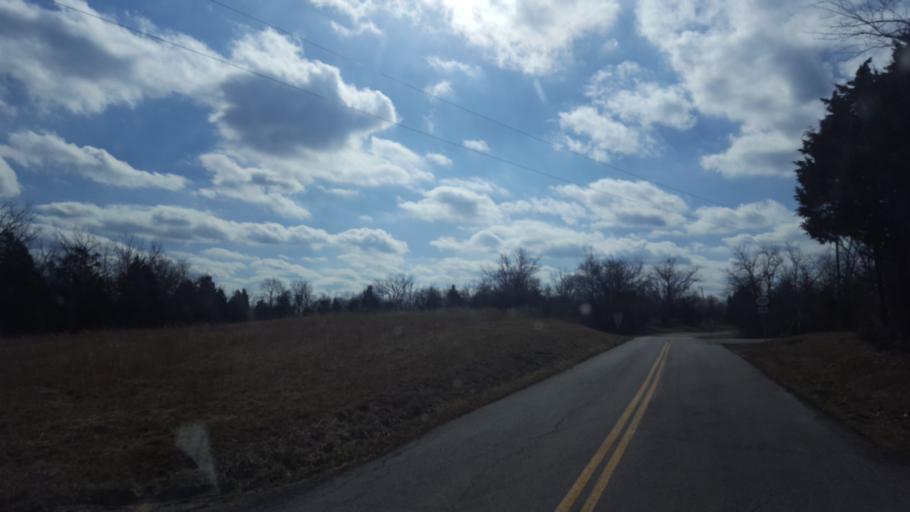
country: US
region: Kentucky
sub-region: Franklin County
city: Frankfort
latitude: 38.3687
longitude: -84.9420
